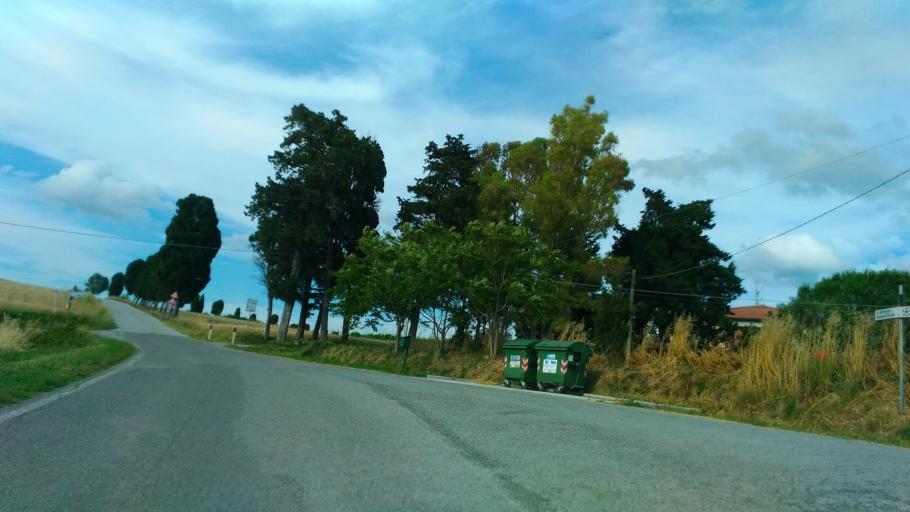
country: IT
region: Tuscany
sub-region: Province of Pisa
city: Orciano Pisano
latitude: 43.4530
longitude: 10.5217
